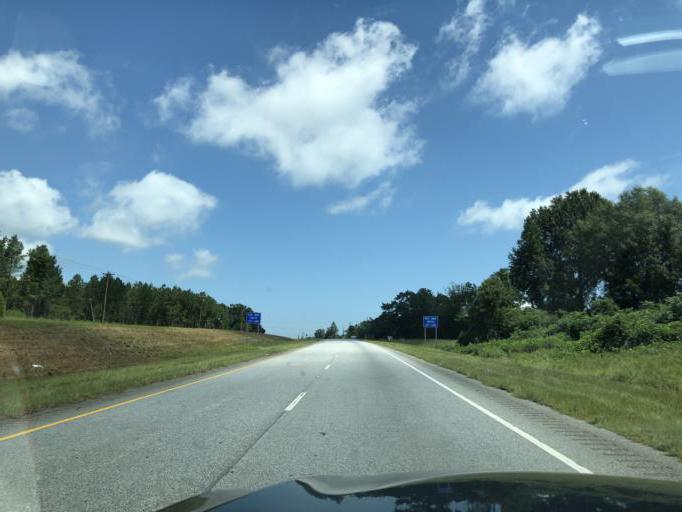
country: US
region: Alabama
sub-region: Barbour County
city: Eufaula
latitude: 31.7750
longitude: -85.1804
